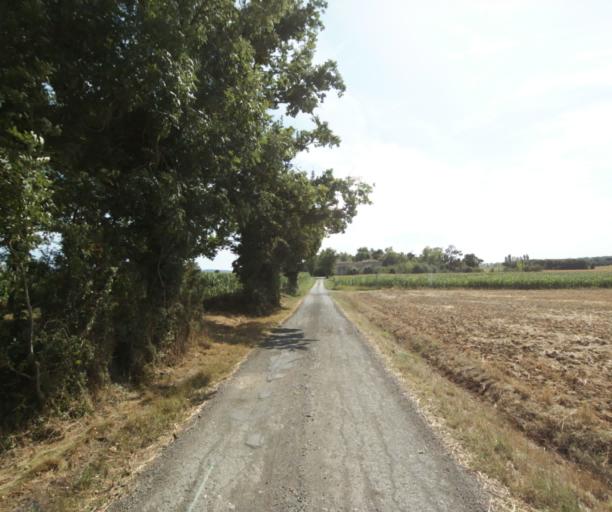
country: FR
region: Midi-Pyrenees
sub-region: Departement du Tarn
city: Soual
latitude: 43.5150
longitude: 2.0891
